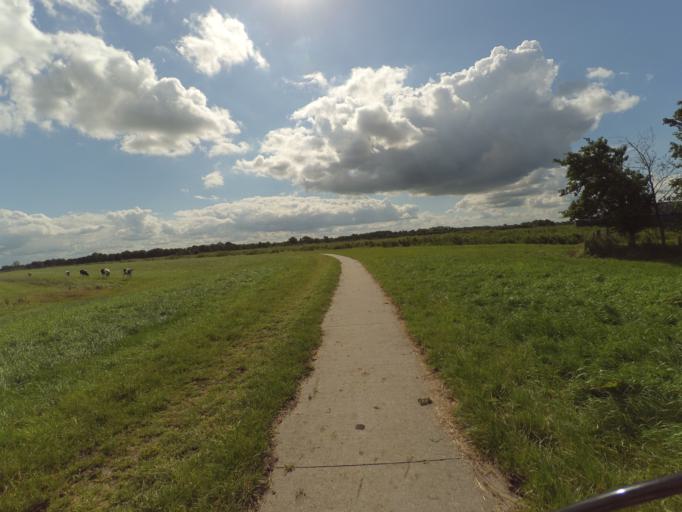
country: NL
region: Friesland
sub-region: Gemeente Tytsjerksteradiel
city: Eastermar
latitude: 53.2001
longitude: 6.0559
